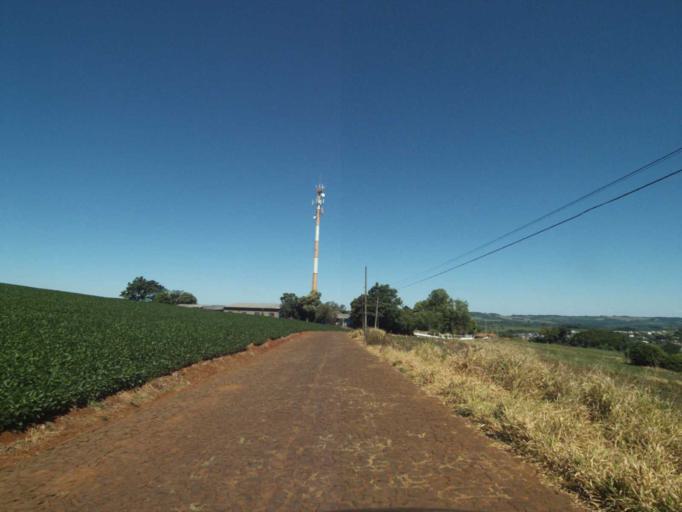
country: BR
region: Parana
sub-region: Coronel Vivida
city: Coronel Vivida
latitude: -25.9596
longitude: -52.8220
